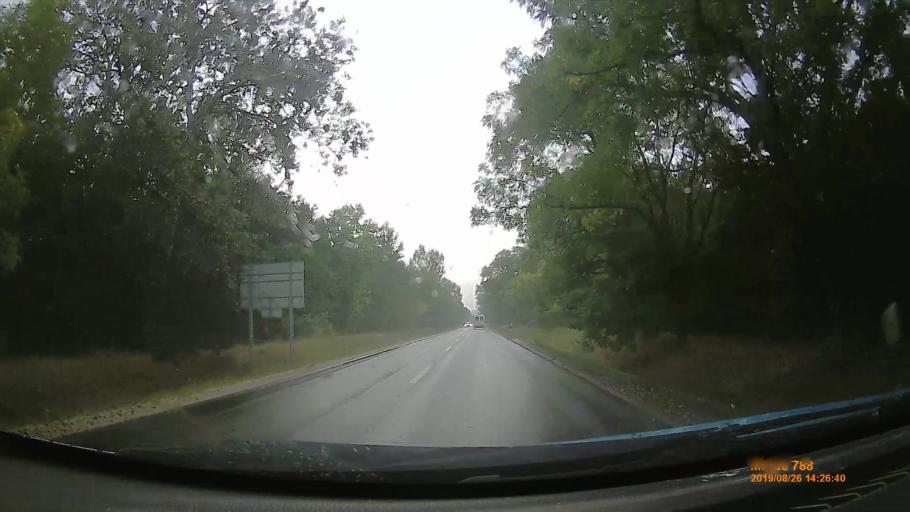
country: HU
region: Fejer
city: Zamoly
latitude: 47.3427
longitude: 18.4032
